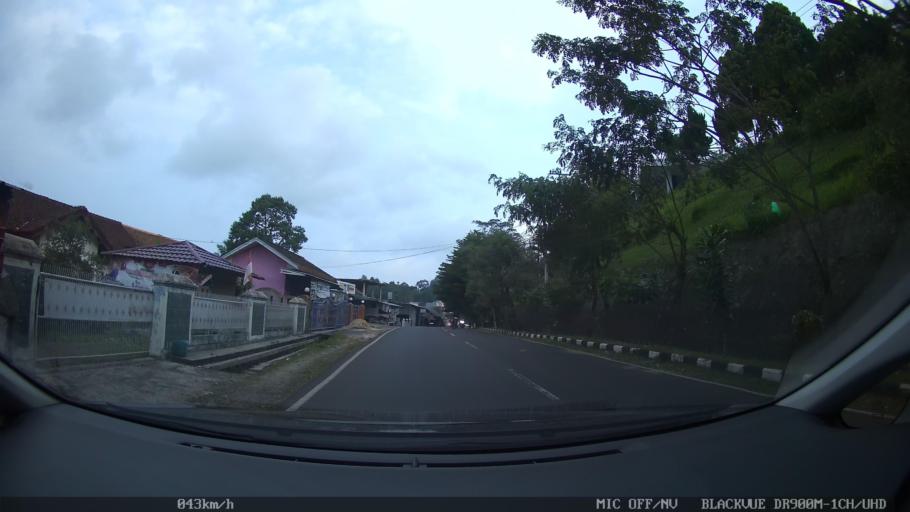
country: ID
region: Lampung
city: Bandarlampung
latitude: -5.4168
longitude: 105.2317
